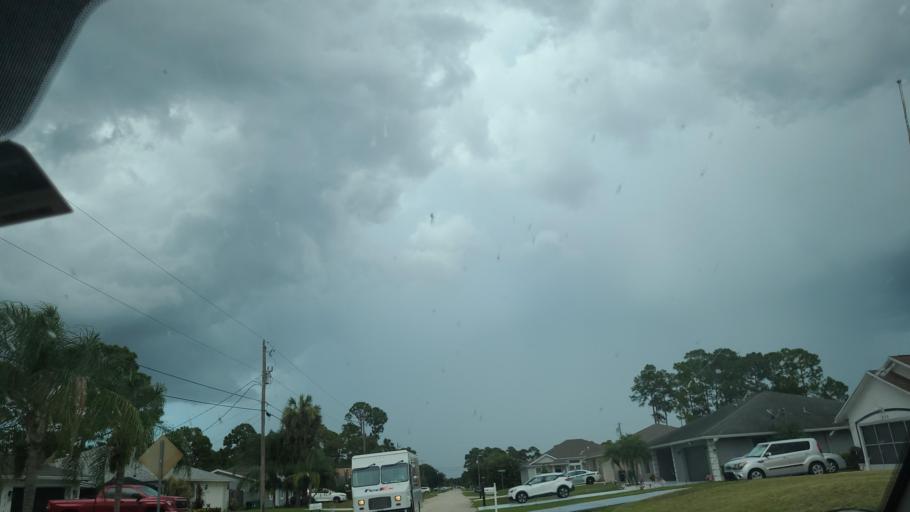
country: US
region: Florida
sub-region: Saint Lucie County
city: Port Saint Lucie
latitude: 27.2529
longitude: -80.4138
